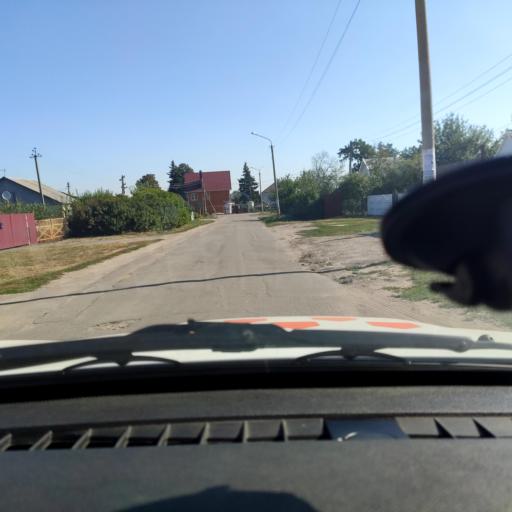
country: RU
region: Voronezj
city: Novaya Usman'
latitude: 51.6234
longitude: 39.3611
